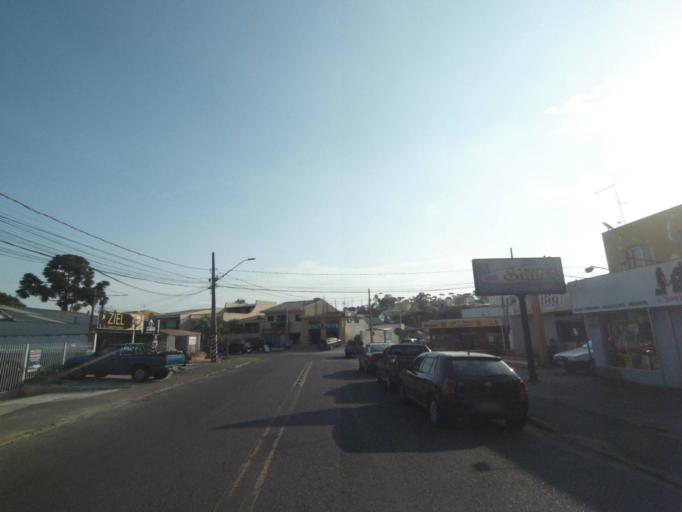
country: BR
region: Parana
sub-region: Curitiba
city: Curitiba
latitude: -25.4866
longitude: -49.3358
